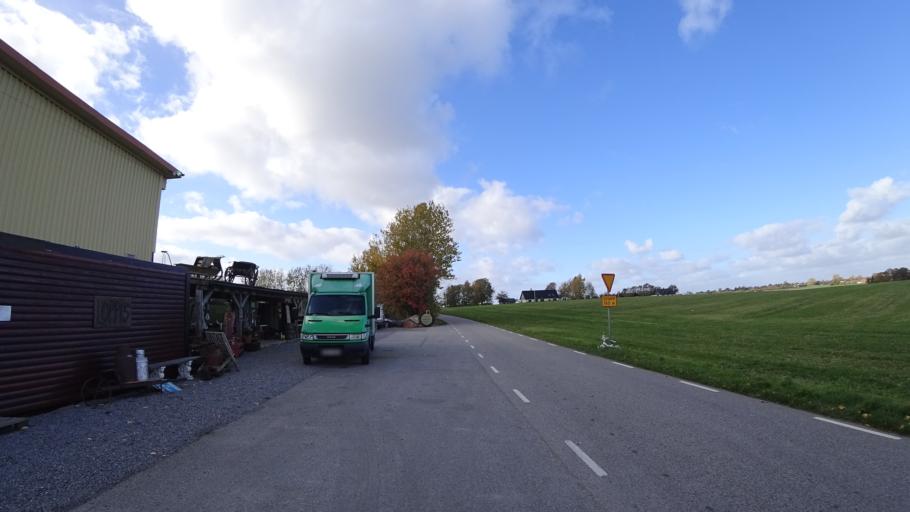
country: SE
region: Skane
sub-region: Staffanstorps Kommun
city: Hjaerup
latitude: 55.6362
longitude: 13.1201
